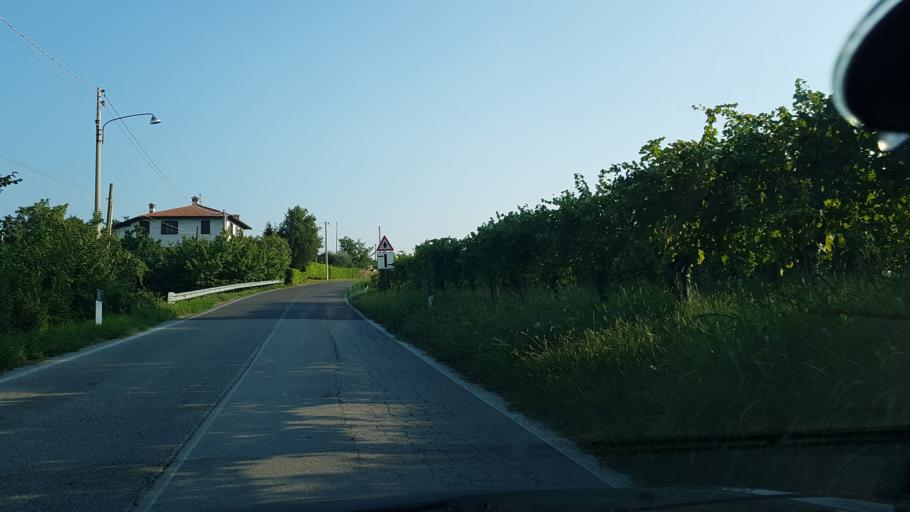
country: IT
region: Friuli Venezia Giulia
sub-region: Provincia di Gorizia
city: San Floriano del Collio
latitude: 45.9794
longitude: 13.6109
